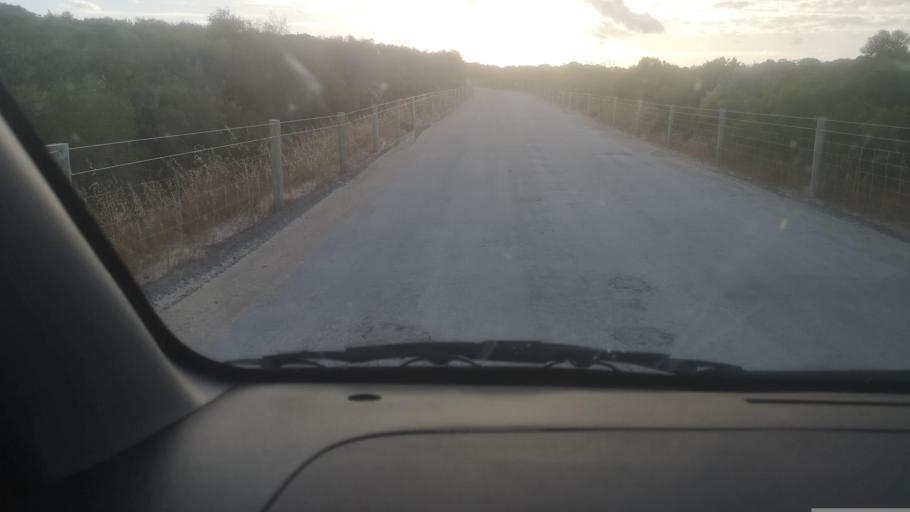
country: AU
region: Western Australia
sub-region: Wanneroo
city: Two Rocks
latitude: -31.5189
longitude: 115.6105
